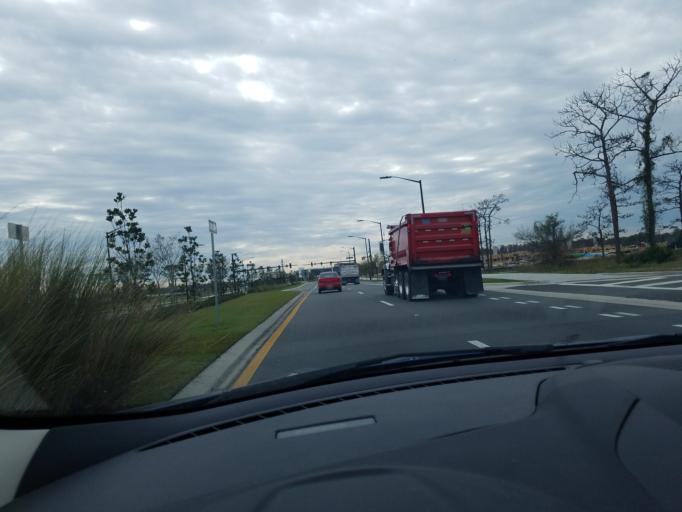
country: US
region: Florida
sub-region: Orange County
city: Hunters Creek
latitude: 28.3467
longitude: -81.3927
